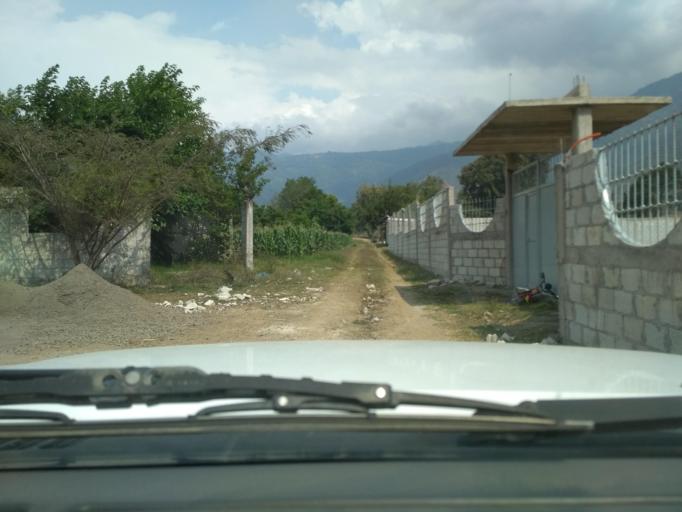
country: MX
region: Veracruz
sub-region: Acultzingo
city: Acatla
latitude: 18.7553
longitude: -97.2290
